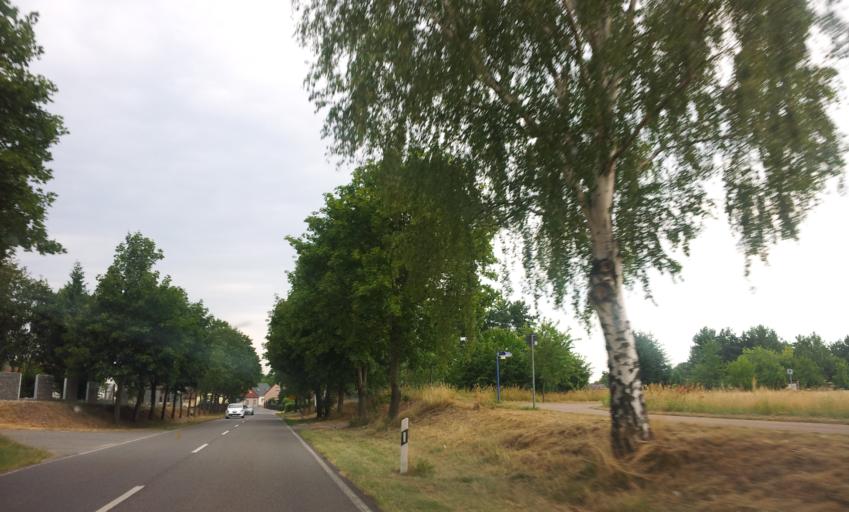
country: DE
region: Brandenburg
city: Juterbog
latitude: 52.0165
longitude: 13.0607
